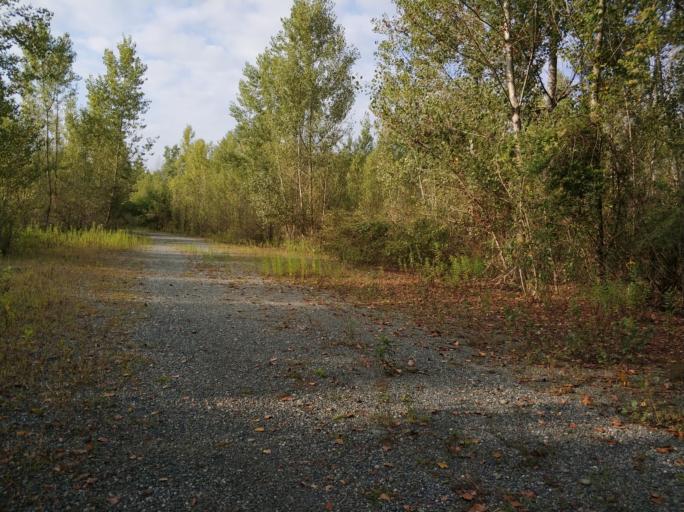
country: IT
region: Piedmont
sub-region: Provincia di Torino
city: Robassomero
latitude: 45.2121
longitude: 7.5695
